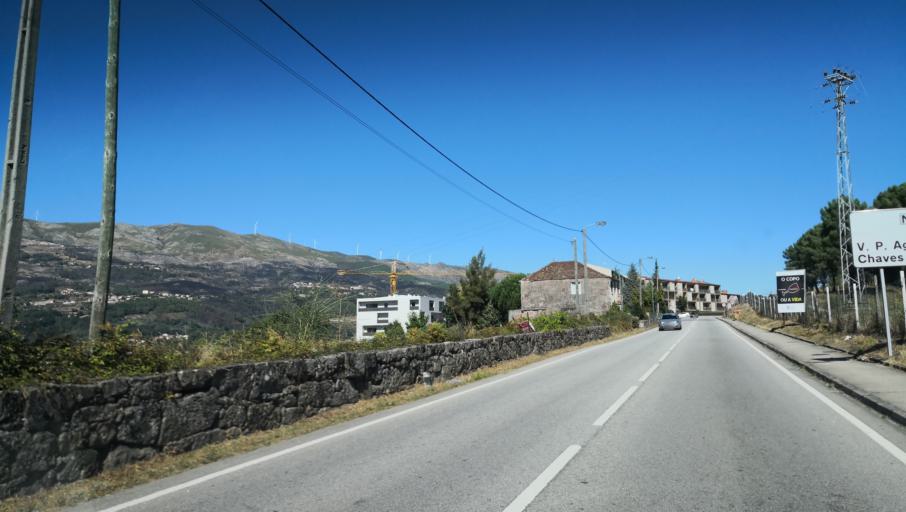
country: PT
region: Vila Real
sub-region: Vila Real
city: Vila Real
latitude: 41.3192
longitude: -7.7323
